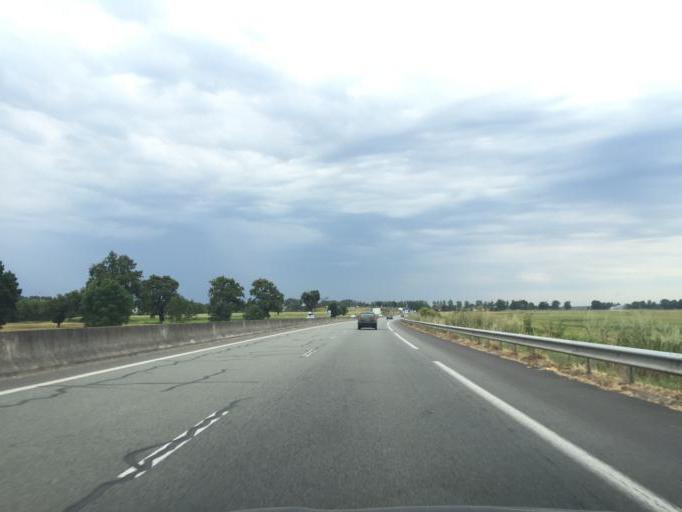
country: FR
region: Auvergne
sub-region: Departement de l'Allier
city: Toulon-sur-Allier
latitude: 46.5106
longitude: 3.3565
